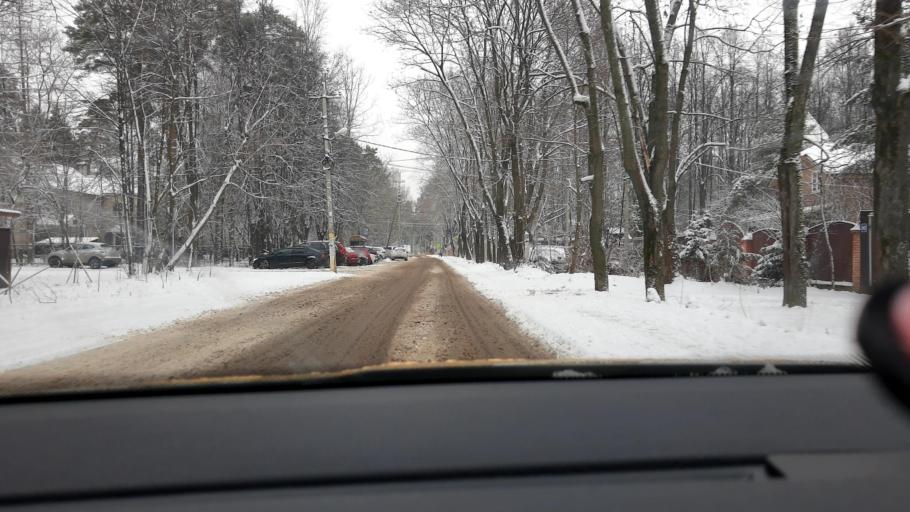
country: RU
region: Moskovskaya
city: Mamontovka
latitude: 55.9825
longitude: 37.8365
